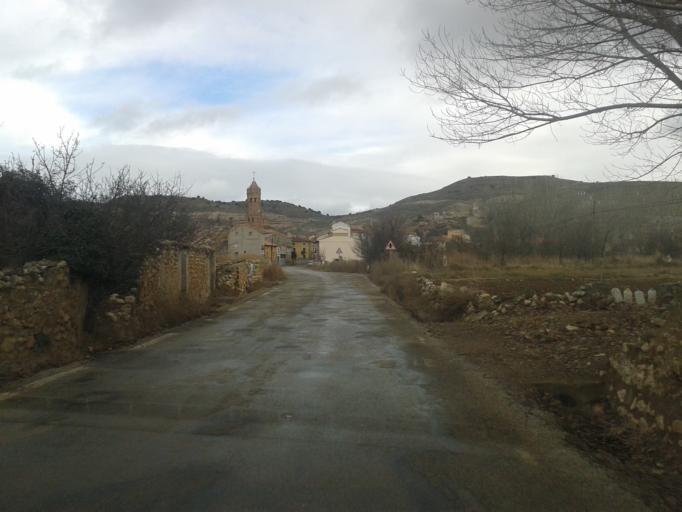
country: ES
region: Aragon
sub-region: Provincia de Teruel
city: Calamocha
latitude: 40.9284
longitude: -1.2595
